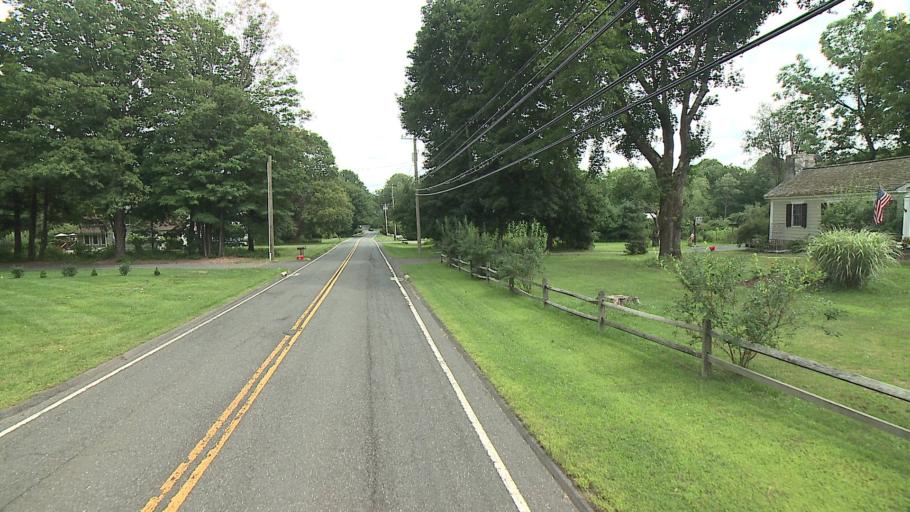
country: US
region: Connecticut
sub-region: Litchfield County
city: Woodbury
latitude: 41.5416
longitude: -73.2255
